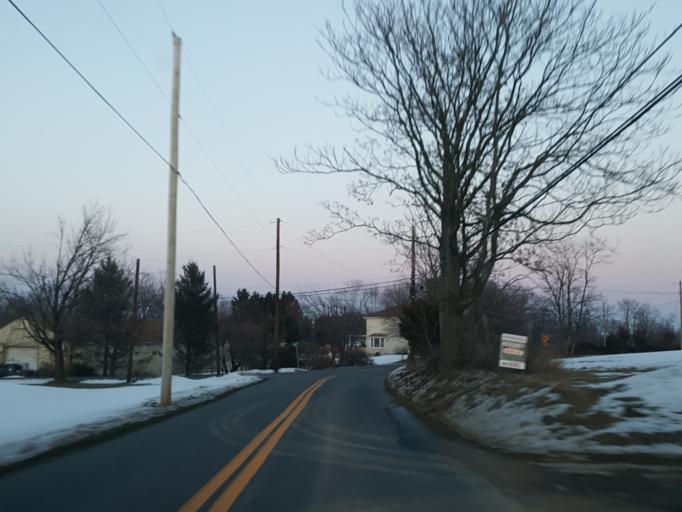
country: US
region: Pennsylvania
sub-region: Dauphin County
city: Skyline View
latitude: 40.3103
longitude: -76.7136
